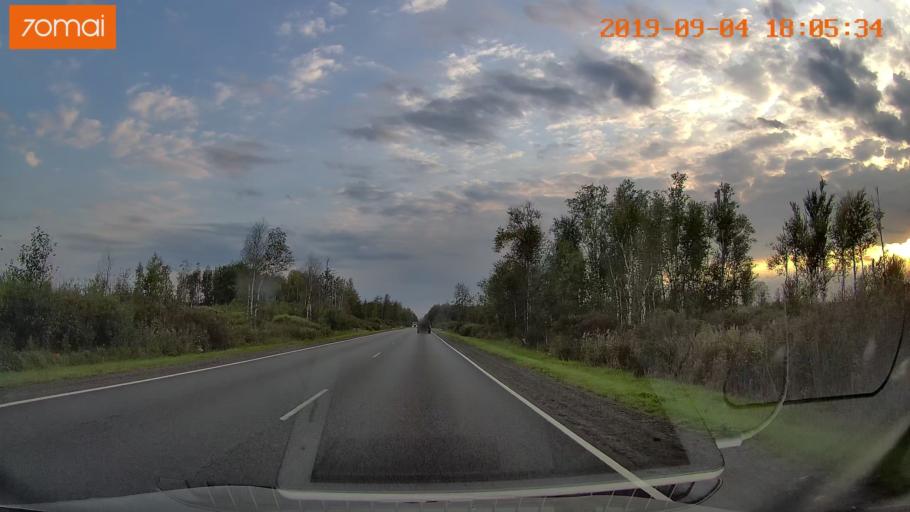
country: RU
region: Moskovskaya
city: Il'inskiy Pogost
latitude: 55.4400
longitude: 38.8250
